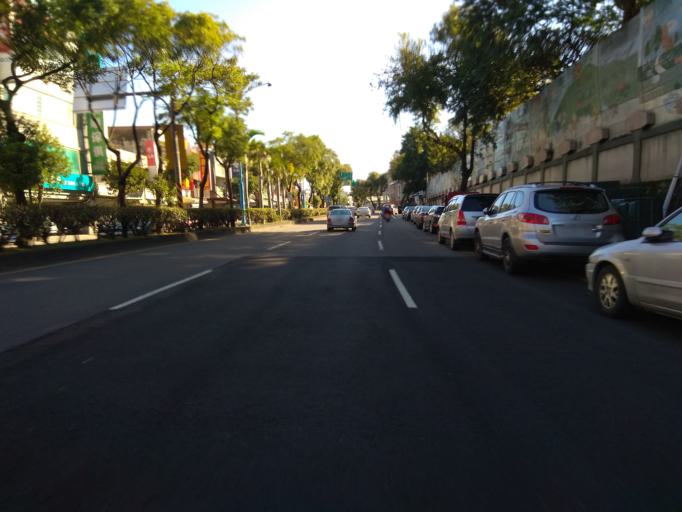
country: TW
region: Taiwan
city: Daxi
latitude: 24.9066
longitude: 121.1444
